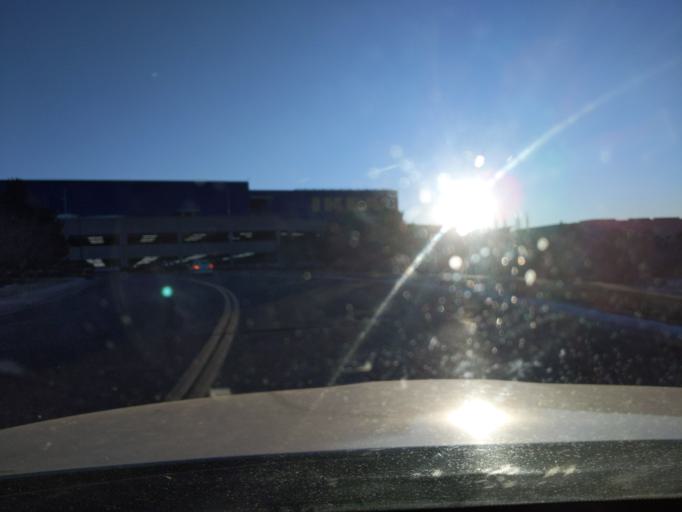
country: US
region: Colorado
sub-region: Arapahoe County
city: Centennial
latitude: 39.5717
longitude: -104.8774
